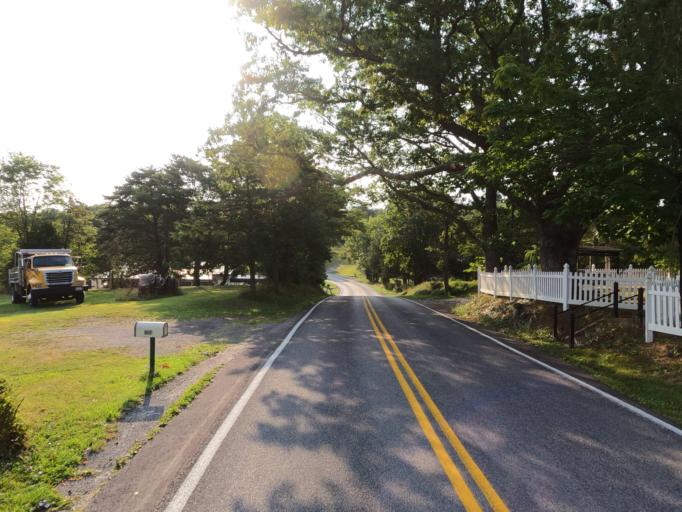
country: US
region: West Virginia
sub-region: Morgan County
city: Berkeley Springs
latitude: 39.6725
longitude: -78.2787
